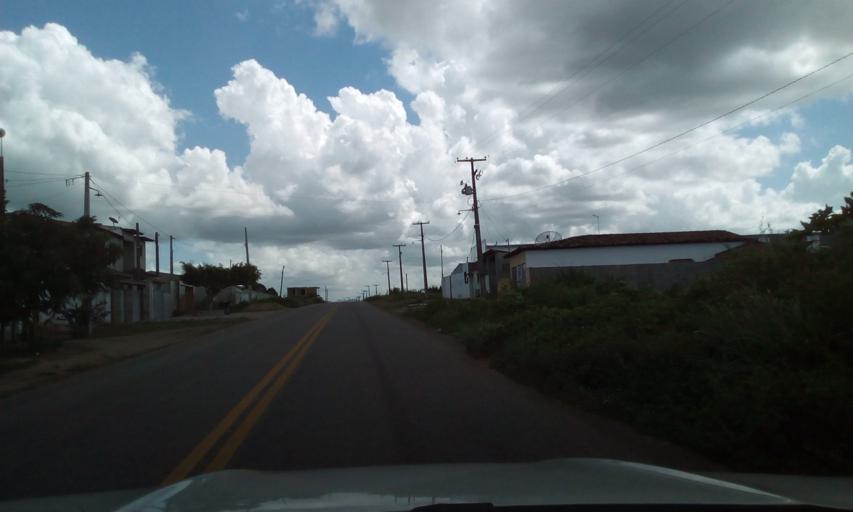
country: BR
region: Paraiba
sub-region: Guarabira
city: Guarabira
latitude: -6.8575
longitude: -35.4409
